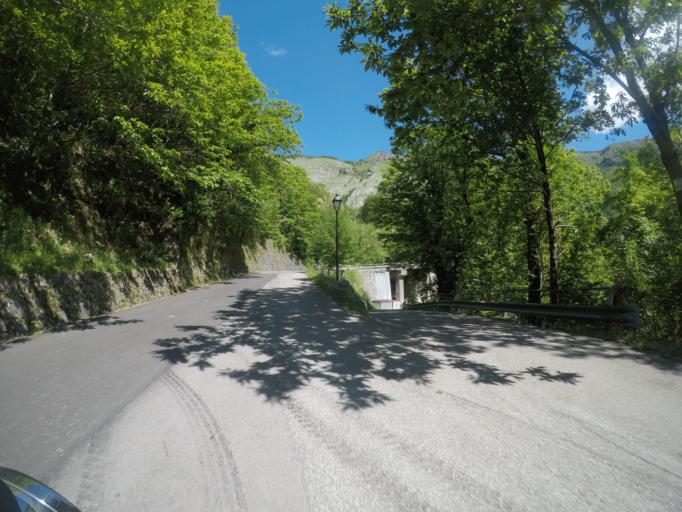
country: IT
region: Tuscany
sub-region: Provincia di Lucca
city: Fontana delle Monache
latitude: 44.0649
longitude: 10.3087
